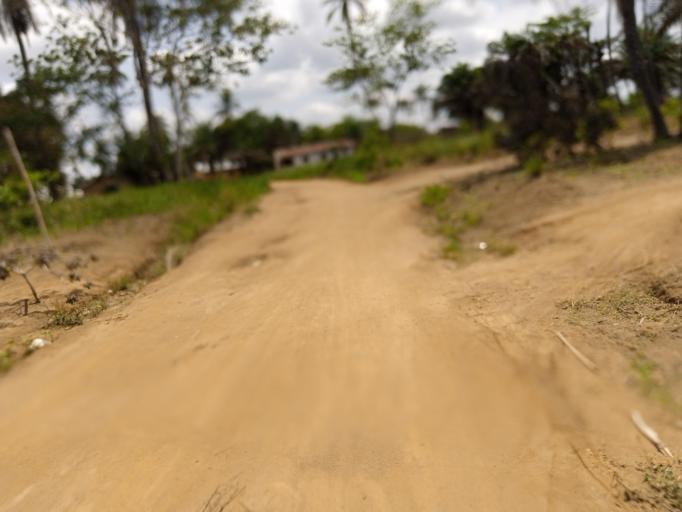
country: SL
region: Western Area
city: Waterloo
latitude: 8.3236
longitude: -13.0120
